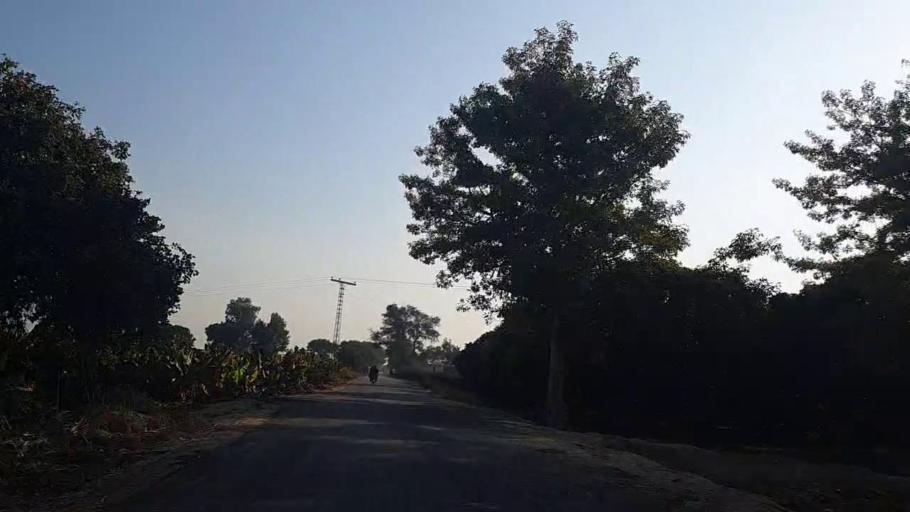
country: PK
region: Sindh
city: Daur
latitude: 26.3303
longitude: 68.1463
